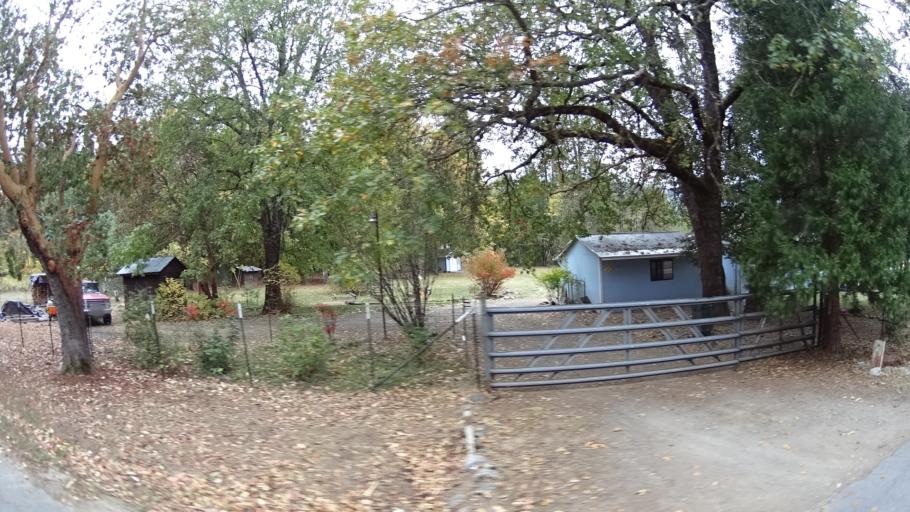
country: US
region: California
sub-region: Siskiyou County
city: Happy Camp
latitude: 41.8376
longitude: -123.1851
